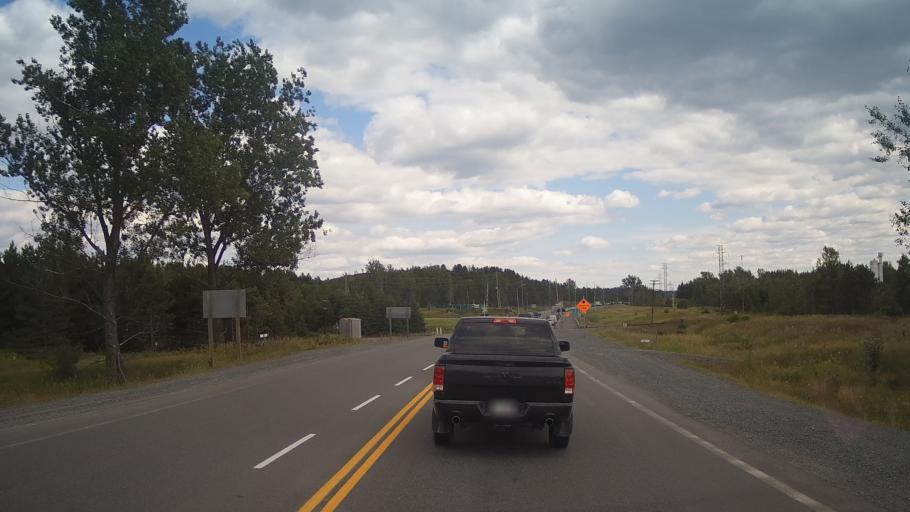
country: CA
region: Ontario
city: Greater Sudbury
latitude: 46.4949
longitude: -80.8447
